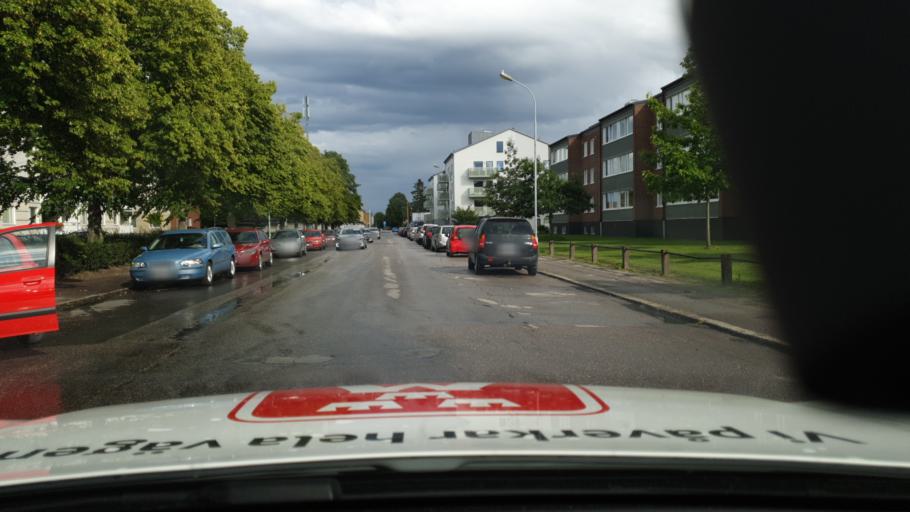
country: SE
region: Vaestra Goetaland
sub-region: Lidkopings Kommun
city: Lidkoping
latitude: 58.5084
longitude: 13.1402
